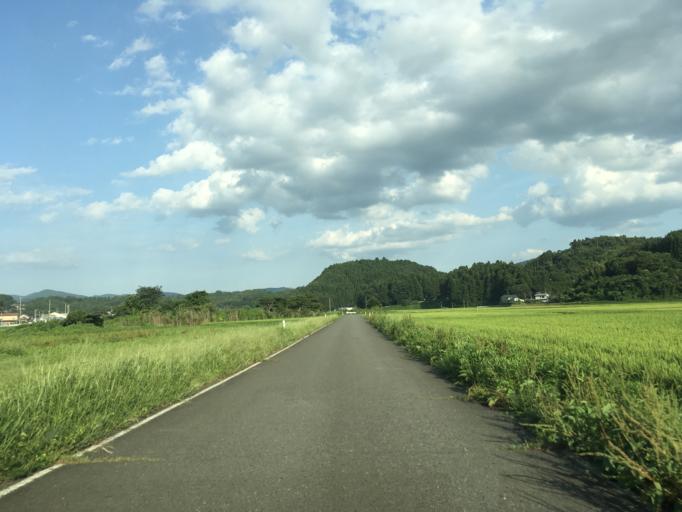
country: JP
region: Iwate
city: Ichinoseki
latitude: 38.8482
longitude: 141.2865
